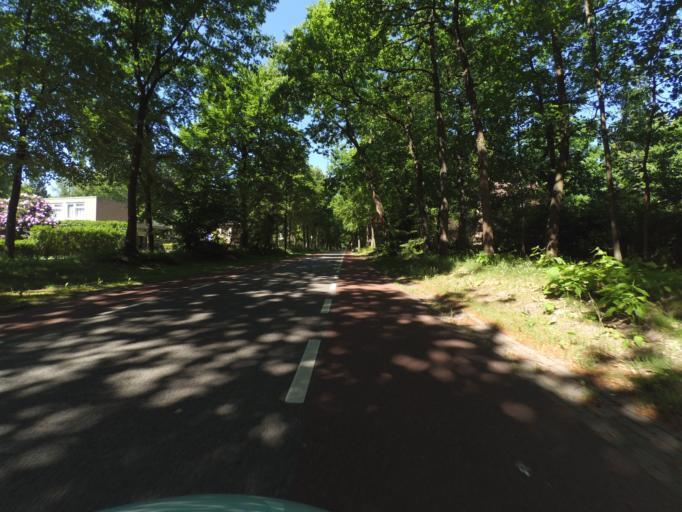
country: NL
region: Gelderland
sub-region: Gemeente Apeldoorn
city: Apeldoorn
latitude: 52.2205
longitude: 5.9276
